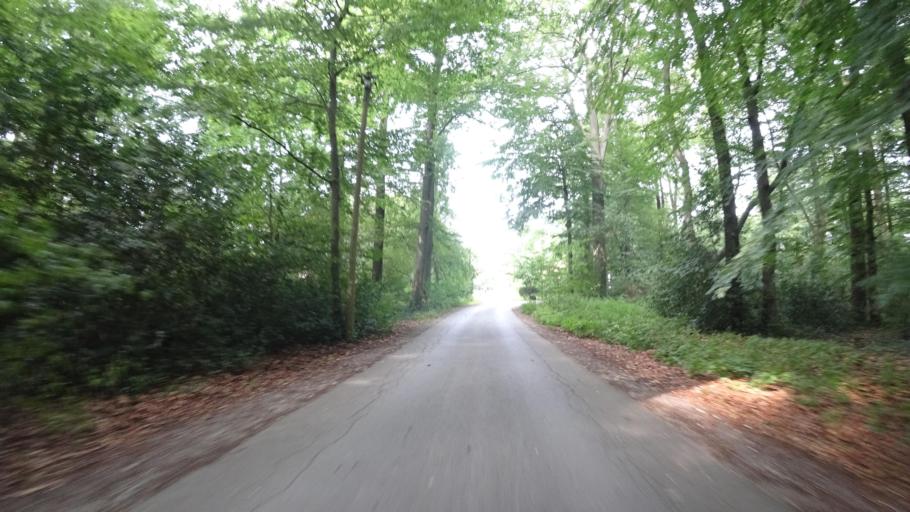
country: DE
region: North Rhine-Westphalia
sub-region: Regierungsbezirk Detmold
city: Guetersloh
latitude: 51.9176
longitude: 8.4383
